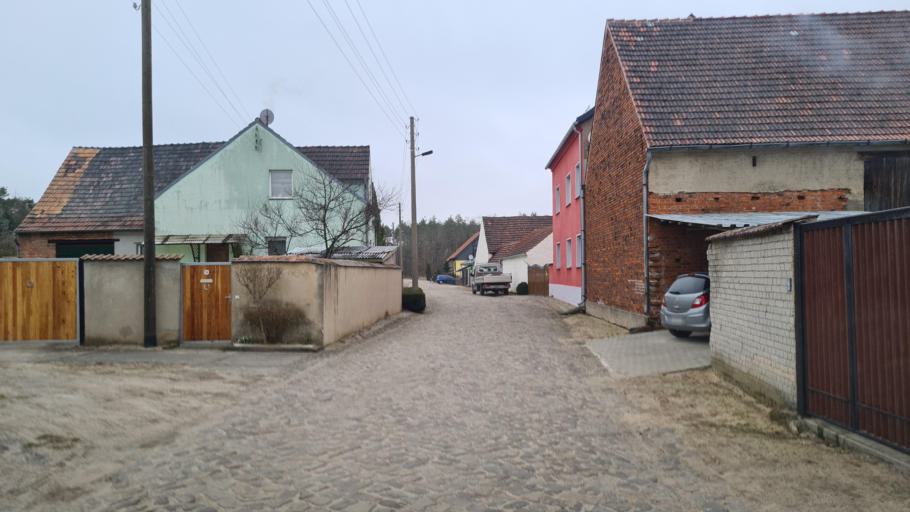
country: DE
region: Brandenburg
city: Herzberg
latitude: 51.6843
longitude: 13.1862
